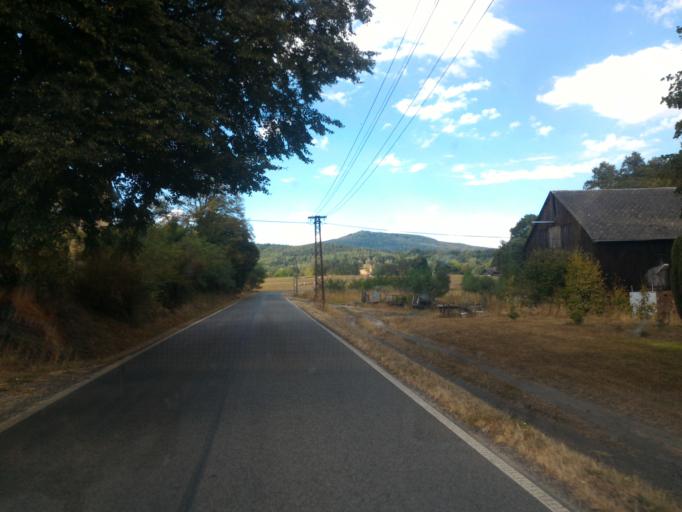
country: CZ
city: Jablonne v Podjestedi
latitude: 50.7859
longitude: 14.7338
